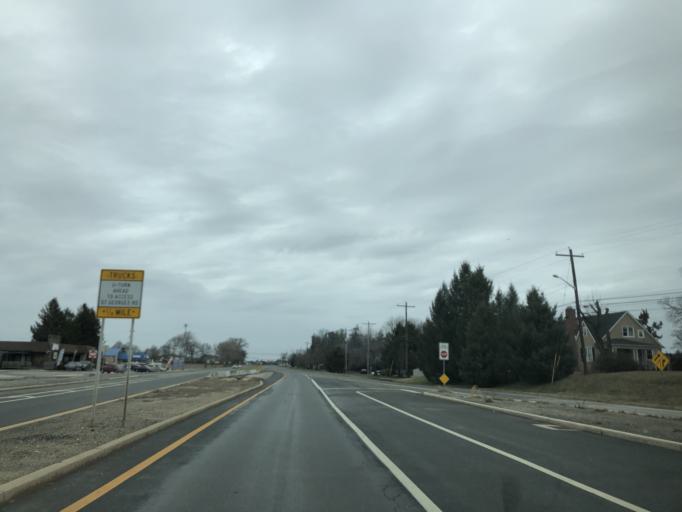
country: US
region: Delaware
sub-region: New Castle County
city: Delaware City
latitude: 39.5586
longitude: -75.6530
